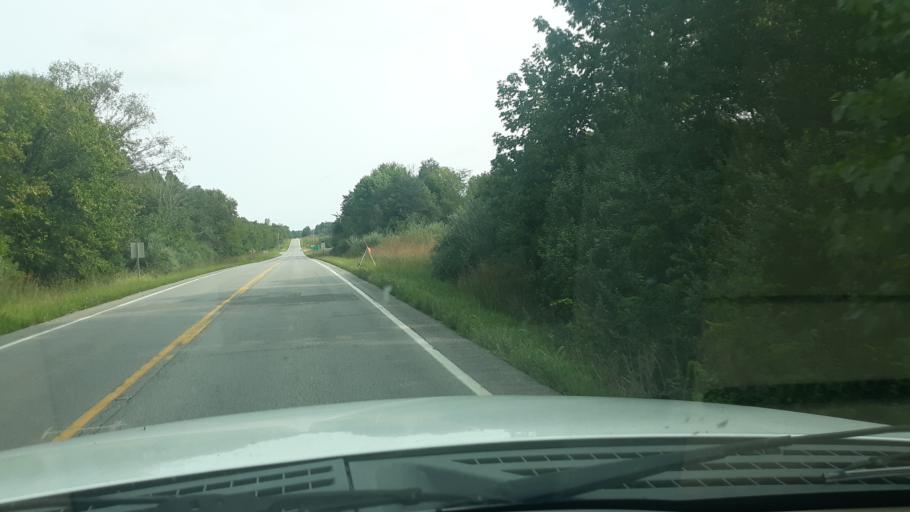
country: US
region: Illinois
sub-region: White County
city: Norris City
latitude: 37.9054
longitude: -88.3585
